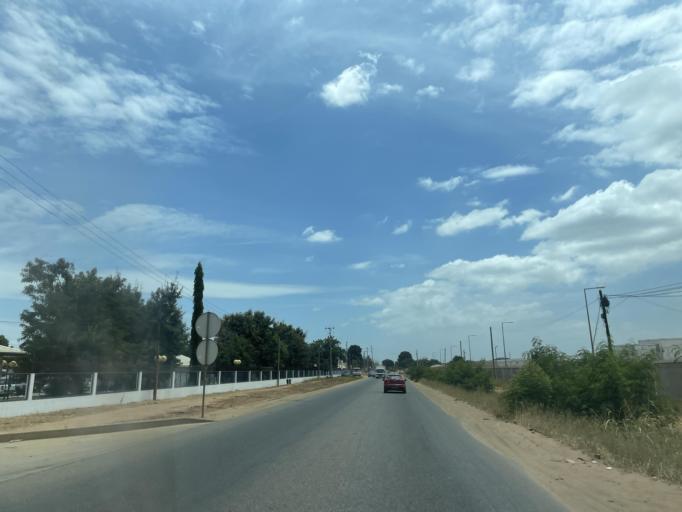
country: AO
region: Luanda
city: Luanda
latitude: -8.9308
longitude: 13.3939
